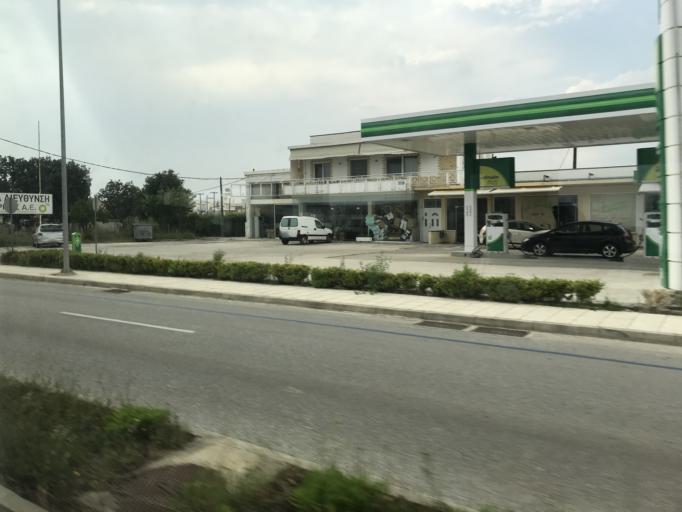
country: GR
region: East Macedonia and Thrace
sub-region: Nomos Evrou
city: Alexandroupoli
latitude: 40.8532
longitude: 25.9109
